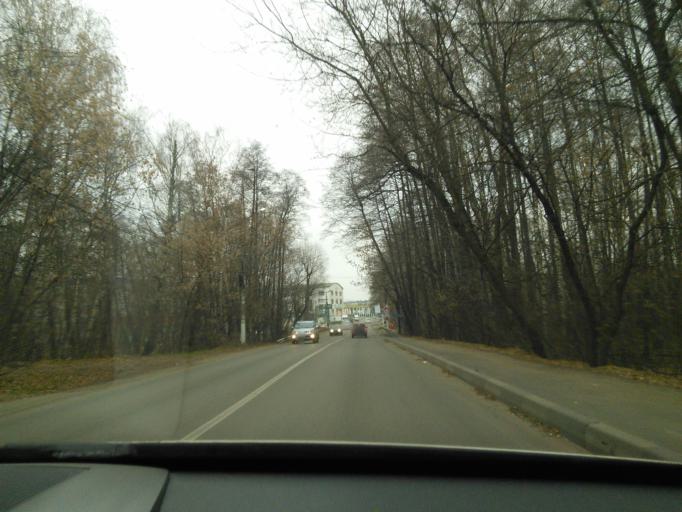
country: RU
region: Moskovskaya
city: Udel'naya
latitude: 55.6336
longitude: 38.0114
